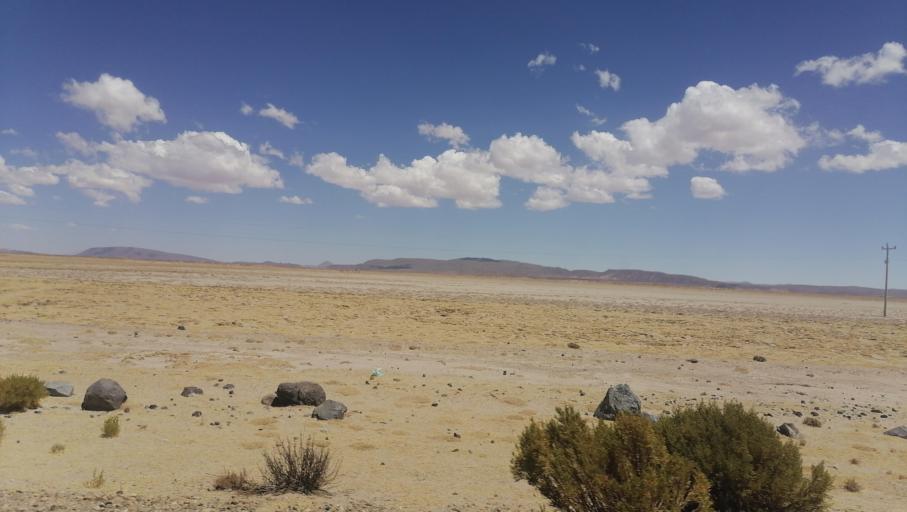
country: BO
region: Oruro
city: Challapata
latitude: -19.2183
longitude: -67.0041
